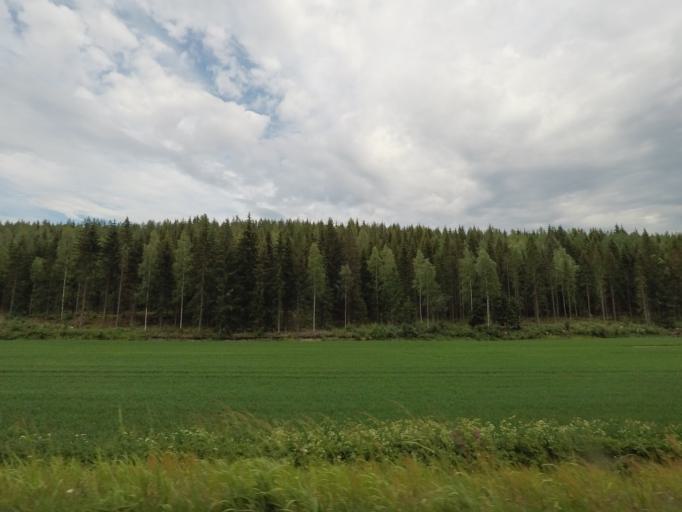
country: FI
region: Uusimaa
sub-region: Porvoo
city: Pukkila
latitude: 60.7891
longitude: 25.4640
